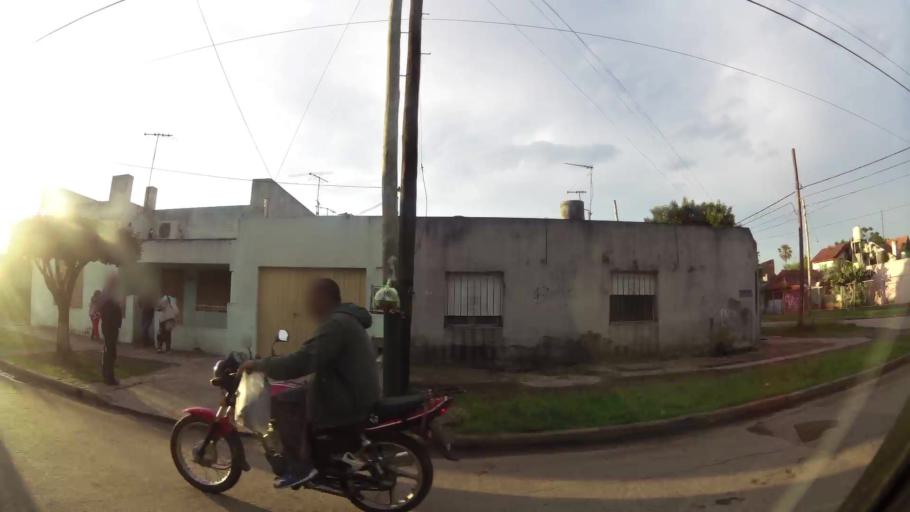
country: AR
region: Buenos Aires
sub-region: Partido de Almirante Brown
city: Adrogue
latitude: -34.7753
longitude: -58.3495
